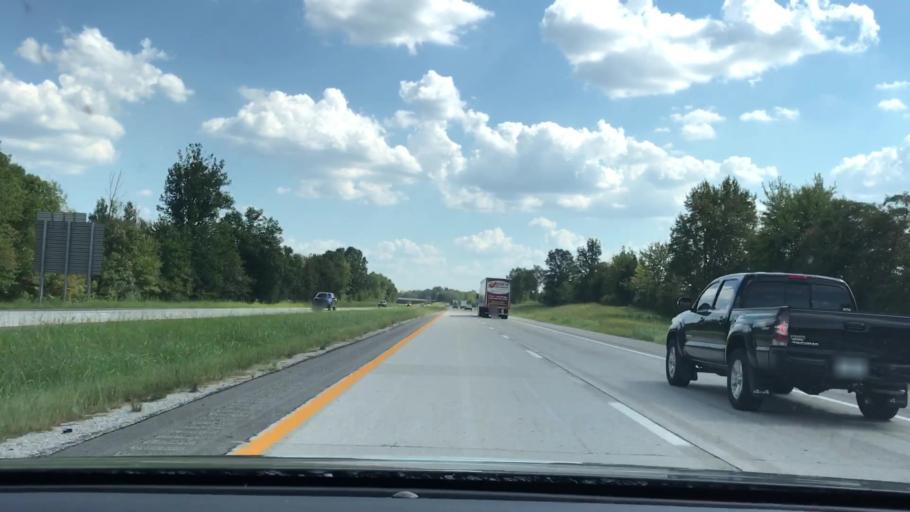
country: US
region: Kentucky
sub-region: Ohio County
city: Oak Grove
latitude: 37.3584
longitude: -86.7916
